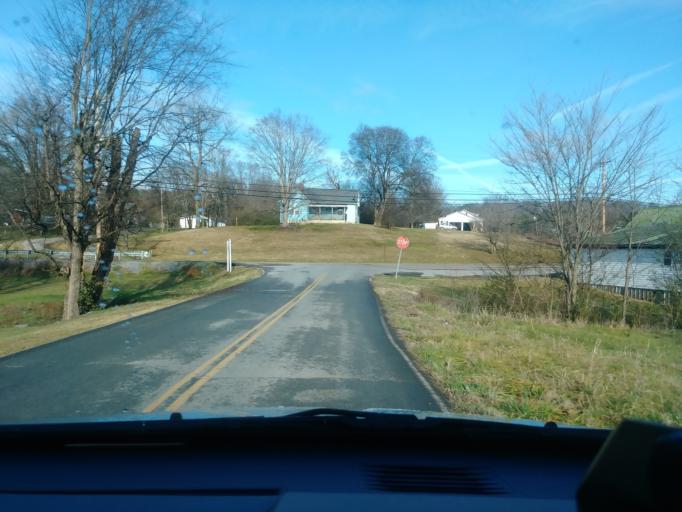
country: US
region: Tennessee
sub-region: Greene County
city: Mosheim
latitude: 36.0998
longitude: -82.9269
